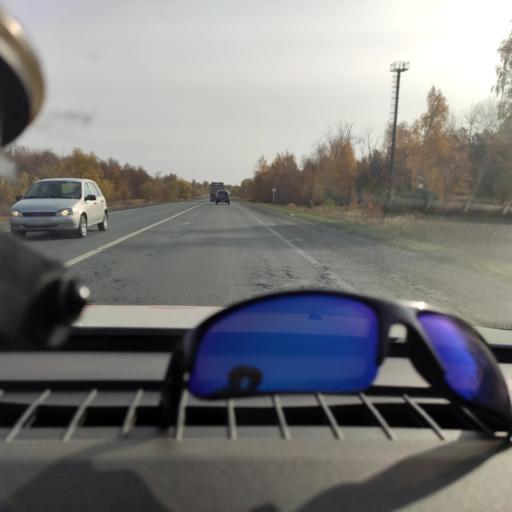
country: RU
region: Samara
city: Chapayevsk
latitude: 52.9929
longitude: 49.8287
